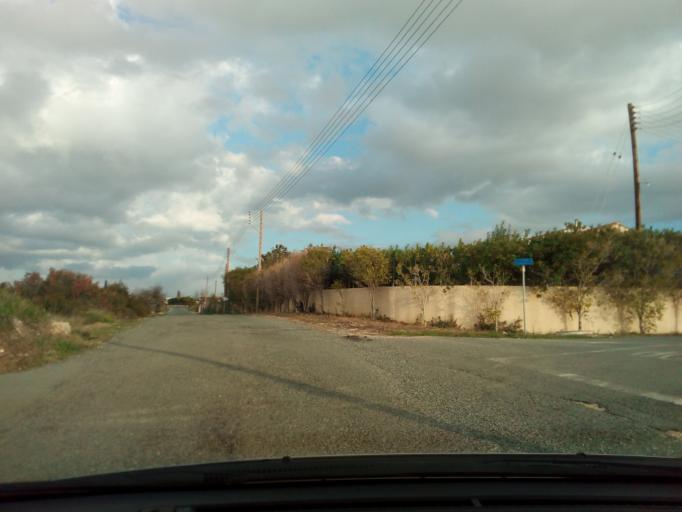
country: CY
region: Pafos
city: Pegeia
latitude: 34.8705
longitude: 32.3687
